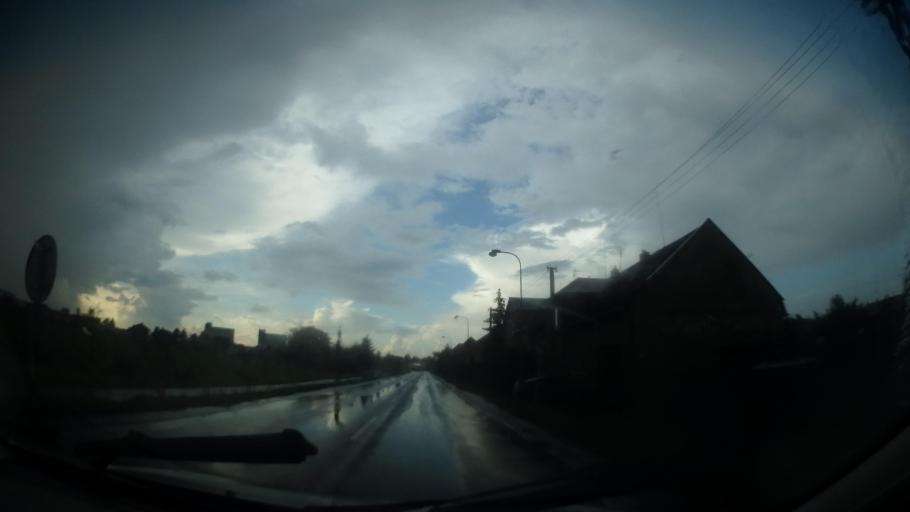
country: CZ
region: Olomoucky
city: Litovel
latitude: 49.6892
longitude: 17.0772
